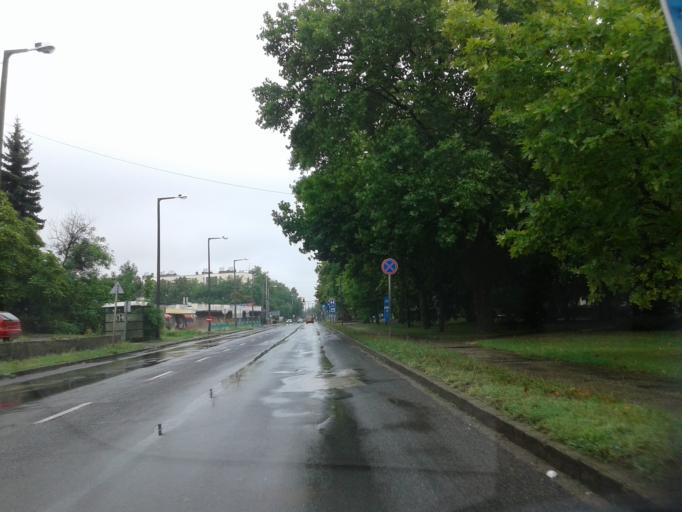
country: HU
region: Bacs-Kiskun
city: Kiskunhalas
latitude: 46.4333
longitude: 19.4872
